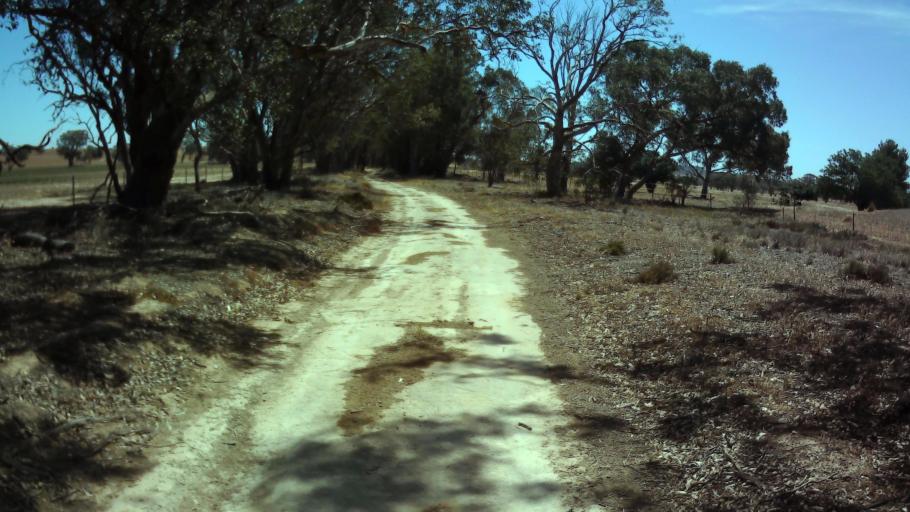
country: AU
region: New South Wales
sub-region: Weddin
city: Grenfell
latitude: -33.9916
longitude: 148.1638
